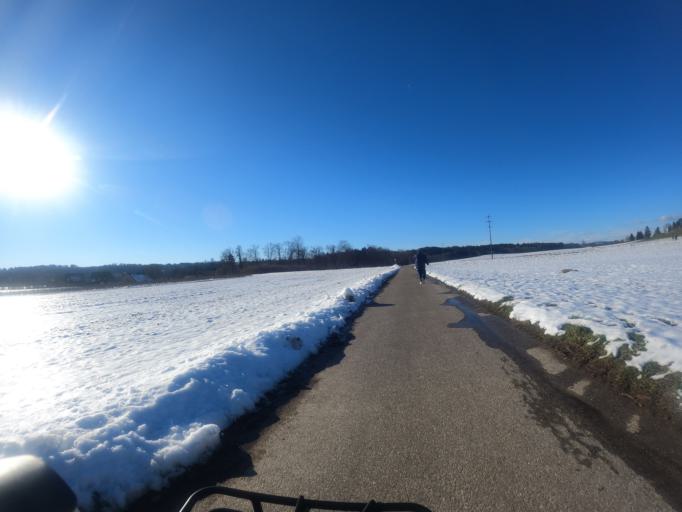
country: CH
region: Aargau
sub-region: Bezirk Bremgarten
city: Berikon
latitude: 47.3342
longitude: 8.3623
